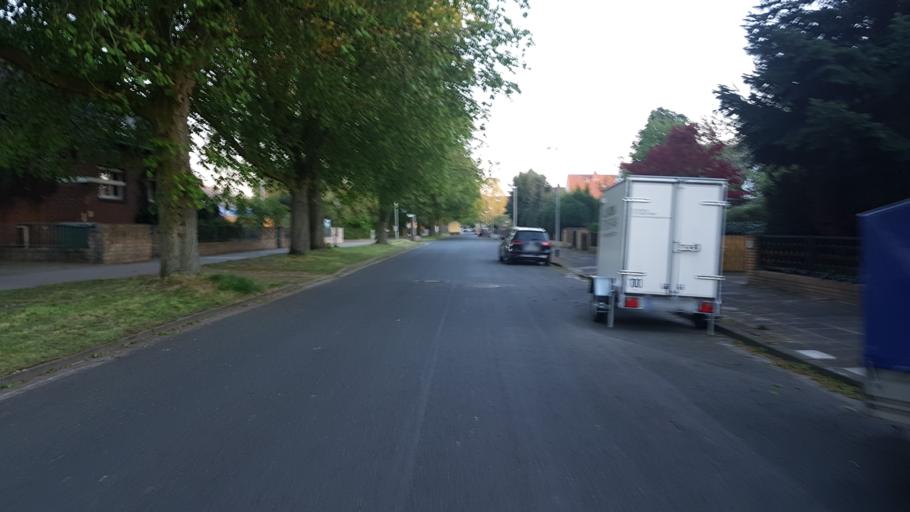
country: DE
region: Lower Saxony
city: Langenhagen
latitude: 52.4197
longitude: 9.7719
